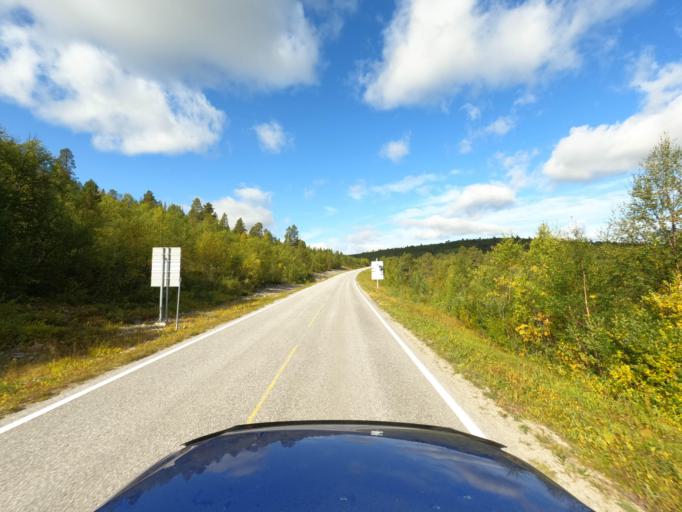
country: NO
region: Finnmark Fylke
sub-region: Karasjok
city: Karasjohka
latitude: 69.4849
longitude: 25.5087
